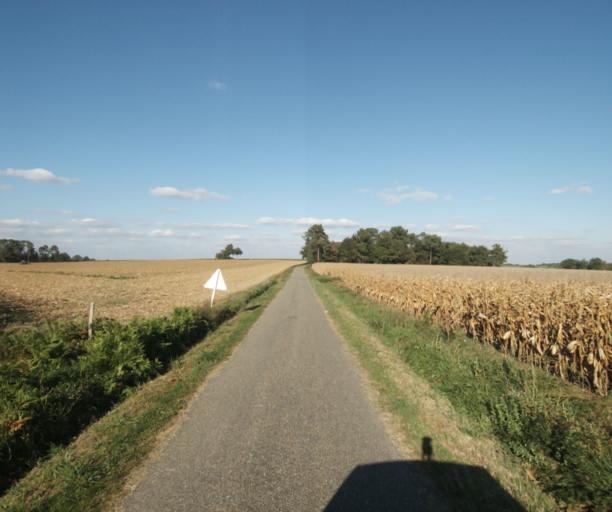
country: FR
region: Midi-Pyrenees
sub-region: Departement du Gers
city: Eauze
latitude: 43.8088
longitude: 0.1365
